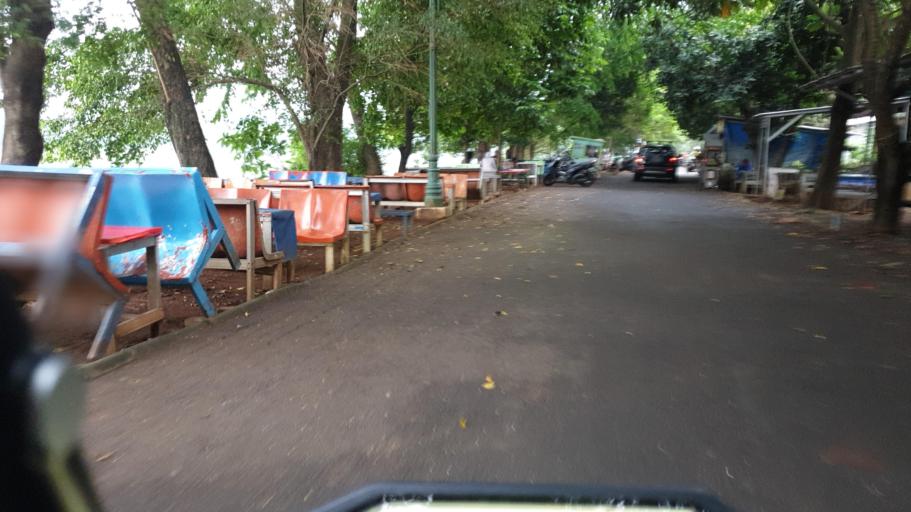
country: ID
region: West Java
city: Depok
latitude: -6.3436
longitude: 106.8229
